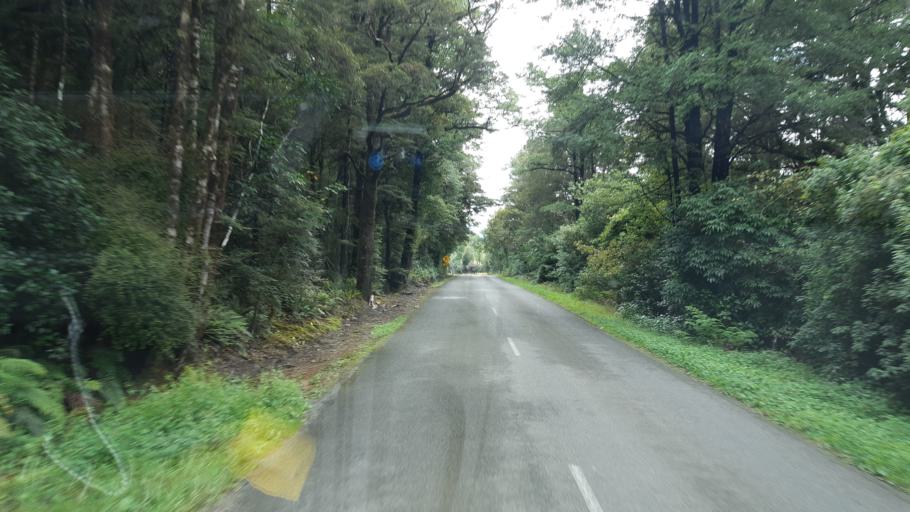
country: NZ
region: West Coast
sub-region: Buller District
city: Westport
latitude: -41.7818
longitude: 172.3705
